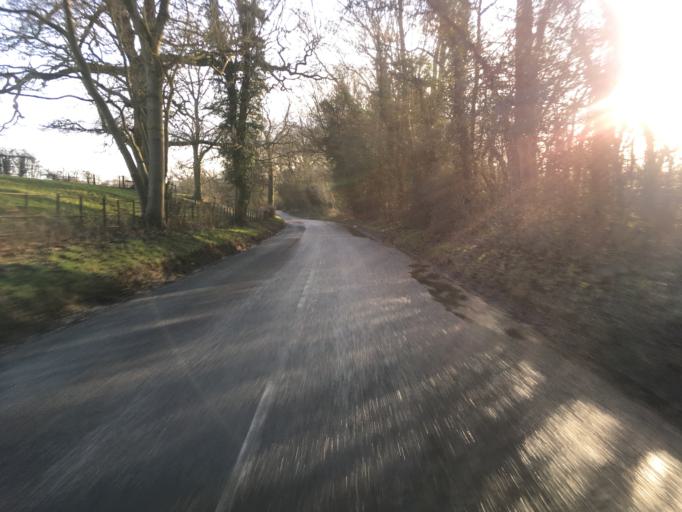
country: GB
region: England
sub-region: Warwickshire
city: Stratford-upon-Avon
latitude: 52.2252
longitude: -1.6895
